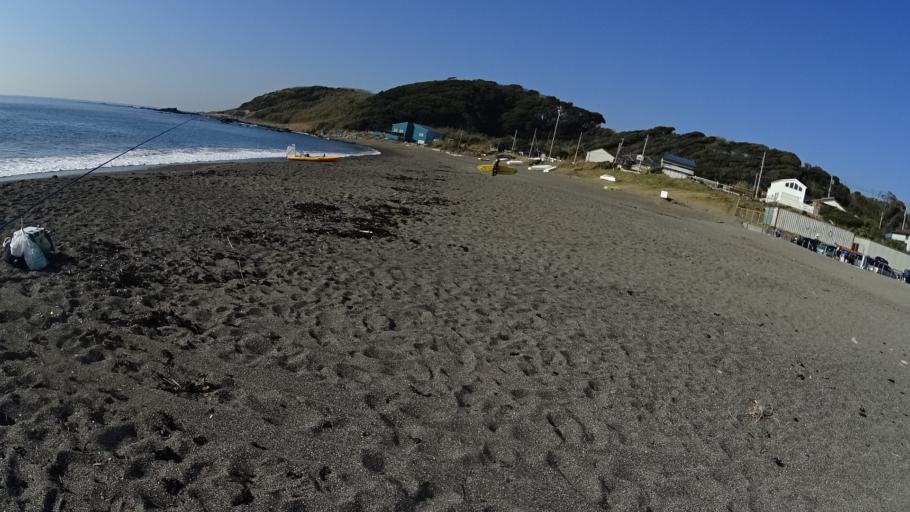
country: JP
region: Kanagawa
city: Miura
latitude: 35.1902
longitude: 139.6158
